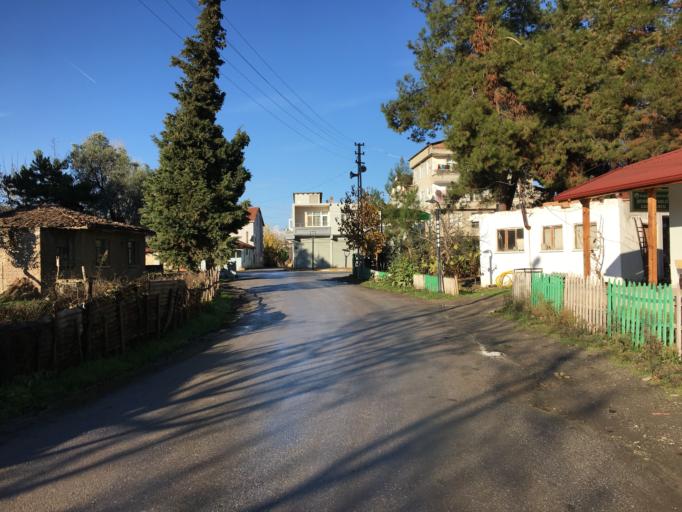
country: TR
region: Samsun
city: Alacam
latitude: 41.6136
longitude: 35.6031
